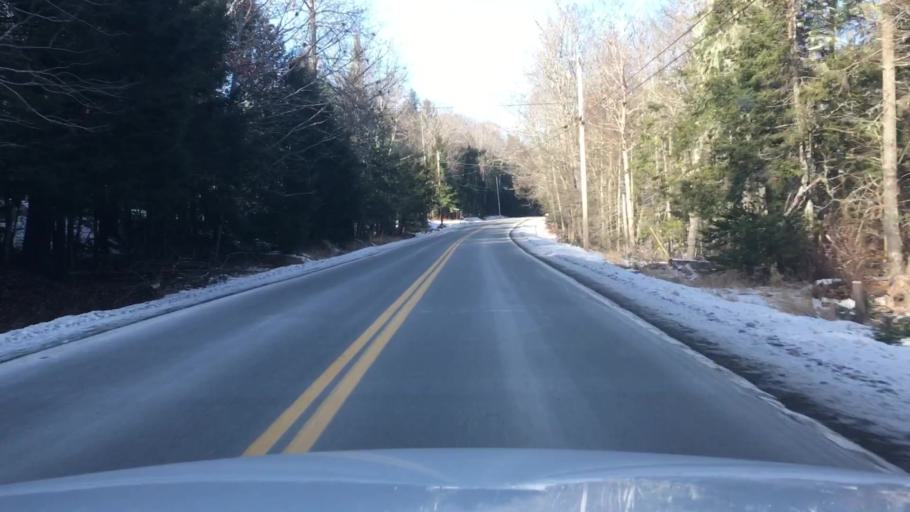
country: US
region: Maine
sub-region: Hancock County
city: Dedham
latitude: 44.6358
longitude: -68.6995
